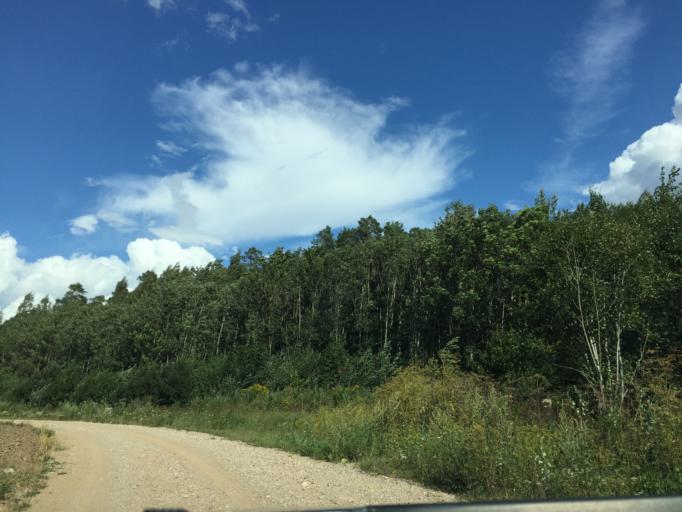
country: LT
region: Siauliu apskritis
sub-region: Joniskis
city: Joniskis
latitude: 56.3550
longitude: 23.5793
